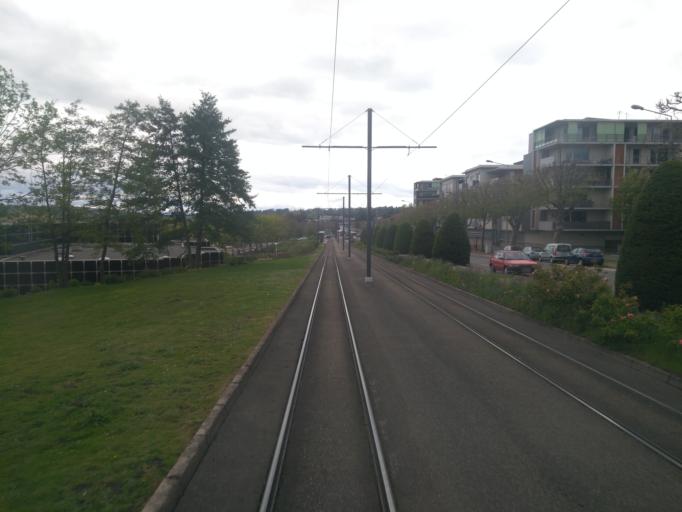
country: FR
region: Rhone-Alpes
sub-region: Departement de la Loire
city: Saint-Priest-en-Jarez
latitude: 45.4694
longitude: 4.3755
